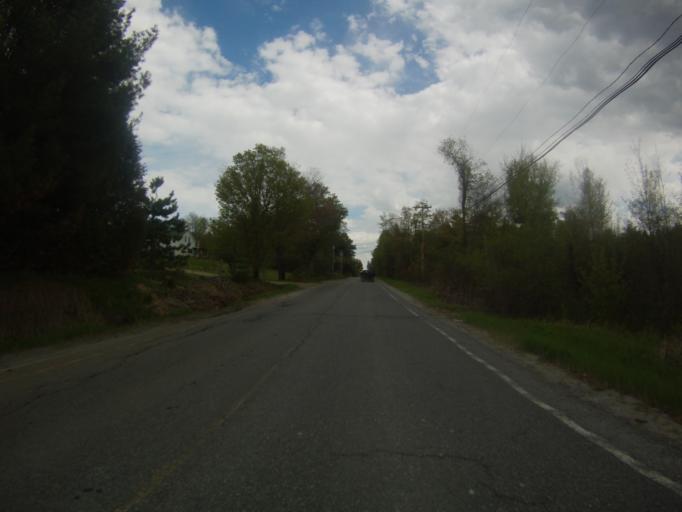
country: US
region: New York
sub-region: Essex County
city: Mineville
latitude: 44.0723
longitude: -73.5235
